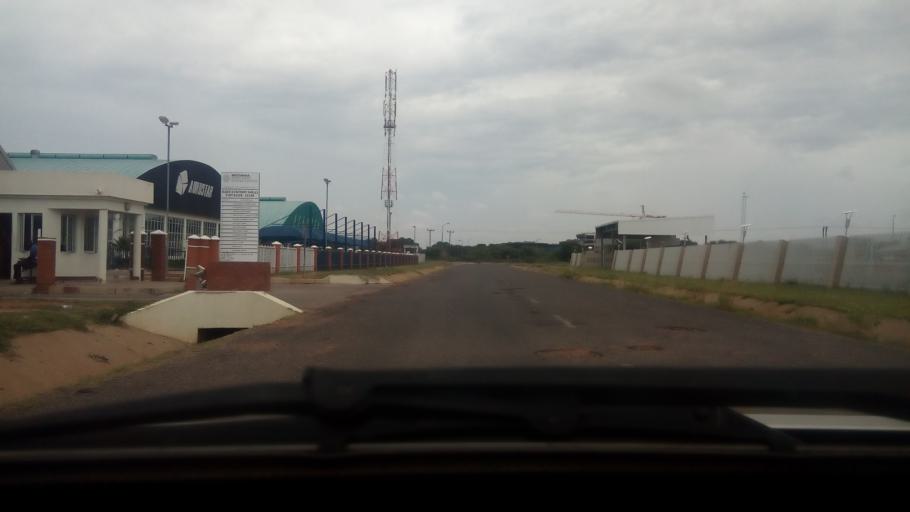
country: BW
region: Kweneng
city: Mmopone
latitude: -24.5883
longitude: 25.9133
